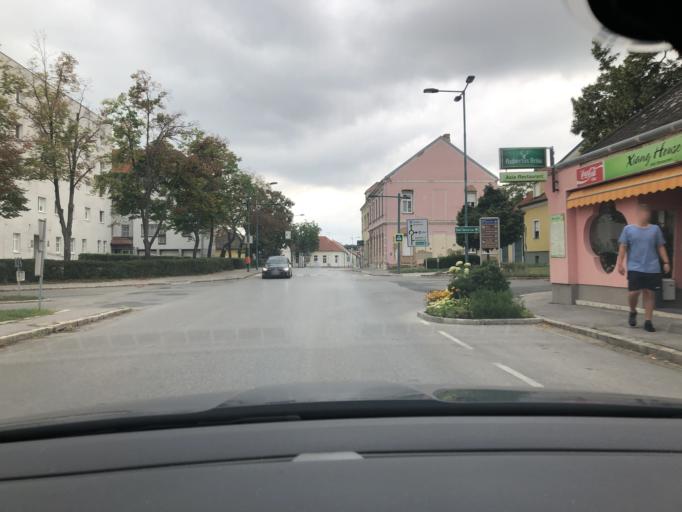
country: AT
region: Lower Austria
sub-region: Politischer Bezirk Mistelbach
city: Laa an der Thaya
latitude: 48.7248
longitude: 16.3840
